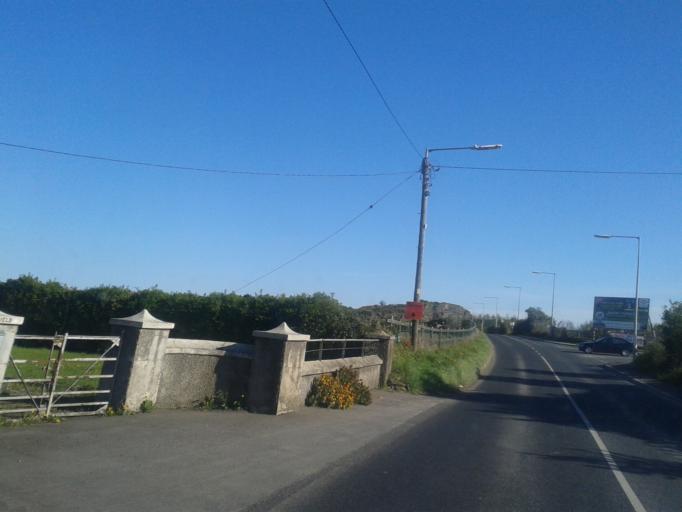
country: IE
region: Leinster
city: Kinsealy-Drinan
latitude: 53.4421
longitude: -6.1942
